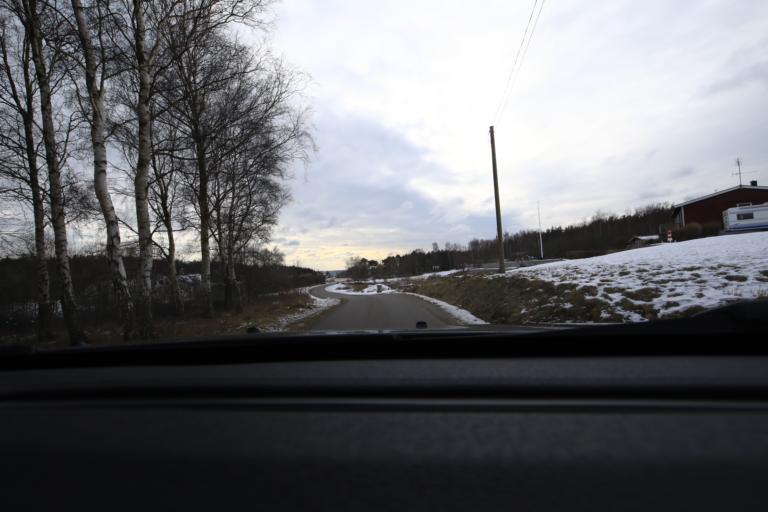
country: SE
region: Halland
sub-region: Kungsbacka Kommun
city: Frillesas
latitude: 57.2211
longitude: 12.1594
